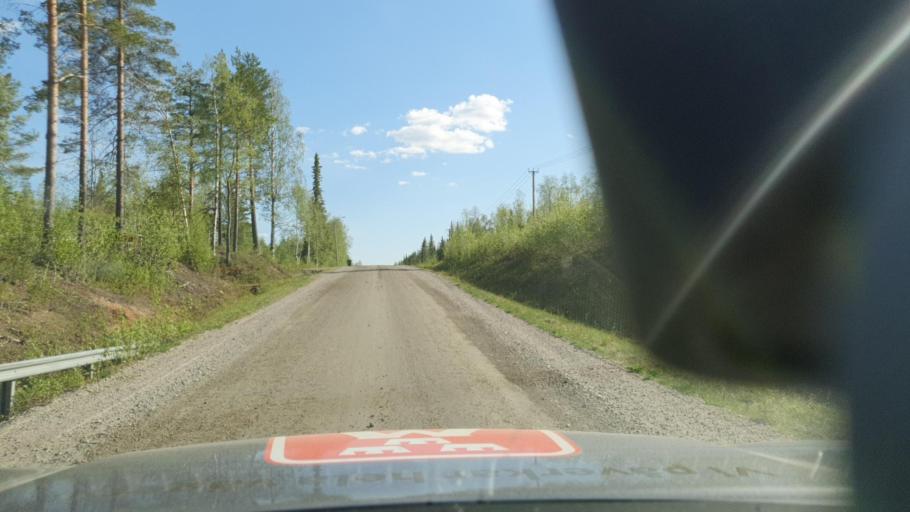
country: SE
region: Norrbotten
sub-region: Bodens Kommun
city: Boden
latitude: 66.5139
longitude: 21.9095
